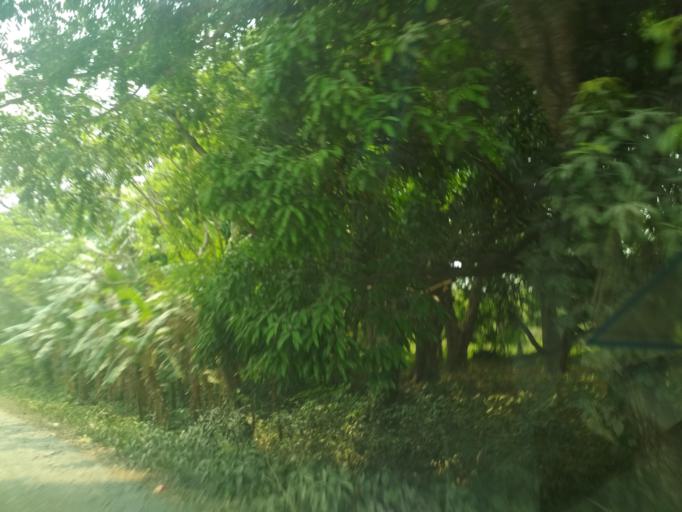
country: MX
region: Veracruz
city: Paso del Toro
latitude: 19.0398
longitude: -96.1521
